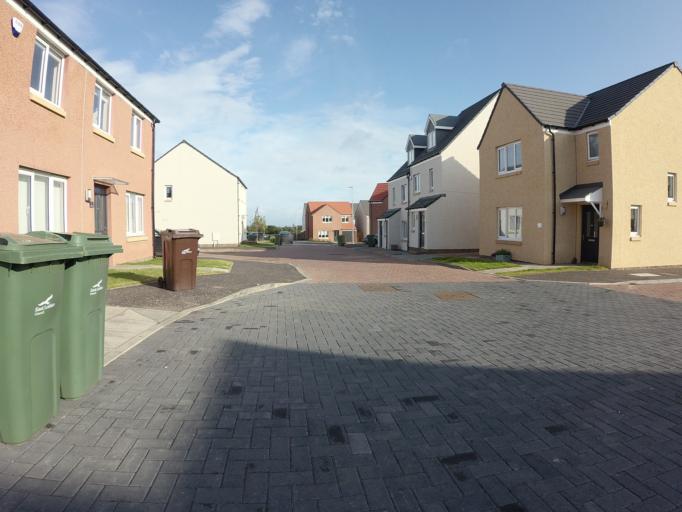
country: GB
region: Scotland
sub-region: East Lothian
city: Prestonpans
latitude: 55.9398
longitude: -3.0019
